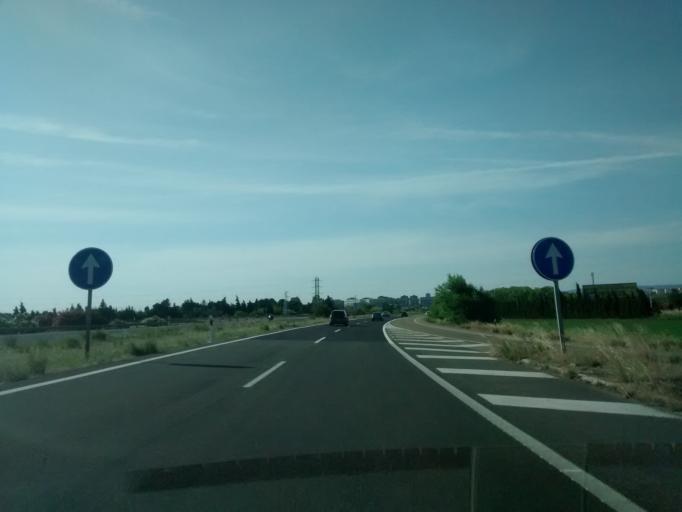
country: ES
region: Aragon
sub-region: Provincia de Zaragoza
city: Almozara
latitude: 41.6734
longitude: -0.9270
